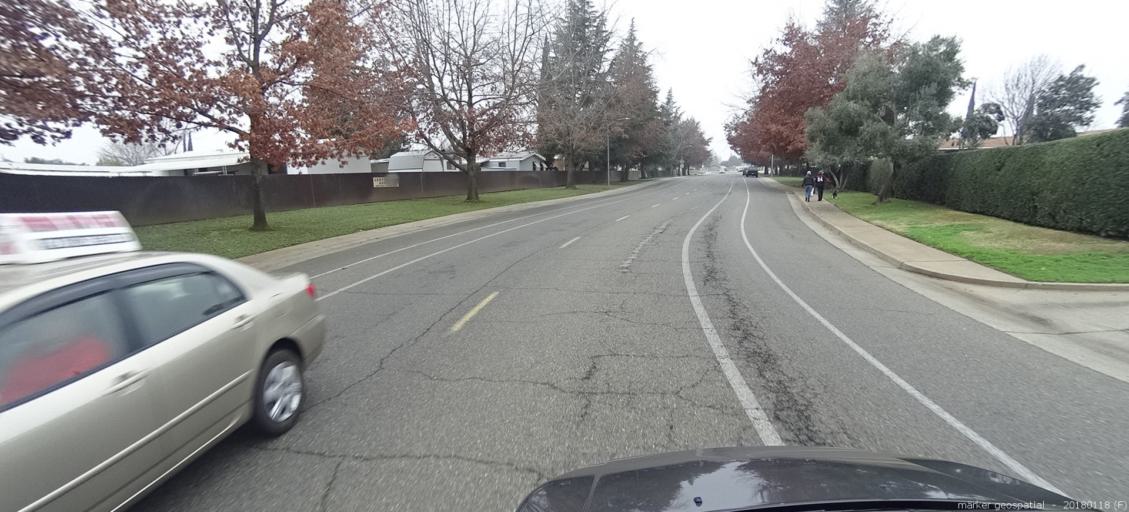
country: US
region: California
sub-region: Sacramento County
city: Rancho Cordova
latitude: 38.5767
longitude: -121.3154
